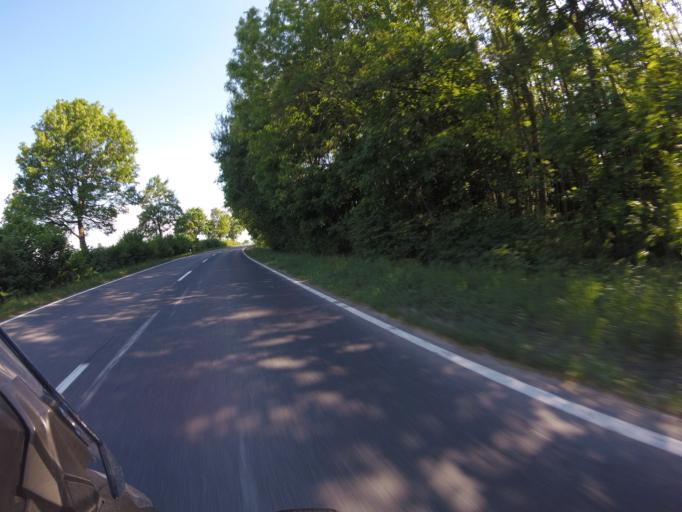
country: DE
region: Bavaria
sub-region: Upper Bavaria
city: Fahrenzhausen
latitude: 48.3673
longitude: 11.5488
